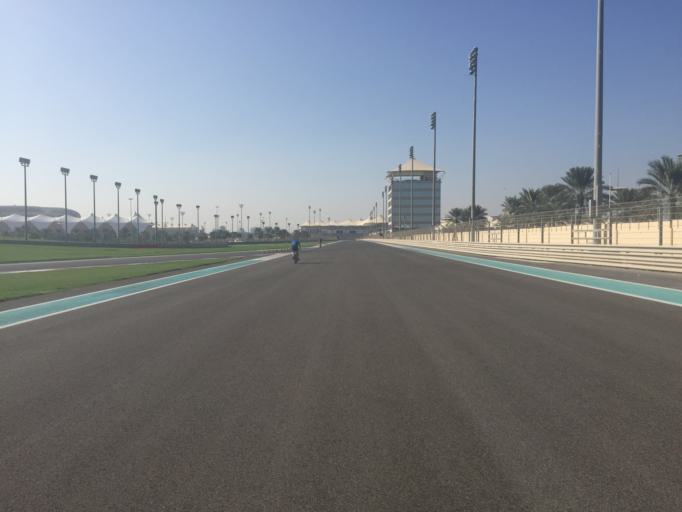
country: AE
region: Abu Dhabi
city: Abu Dhabi
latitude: 24.4755
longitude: 54.6040
